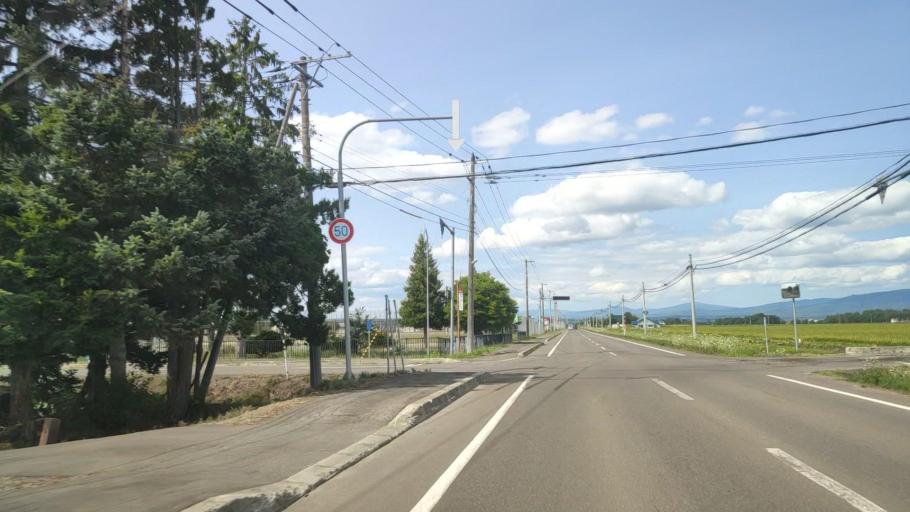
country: JP
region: Hokkaido
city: Nayoro
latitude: 44.2910
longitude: 142.4294
